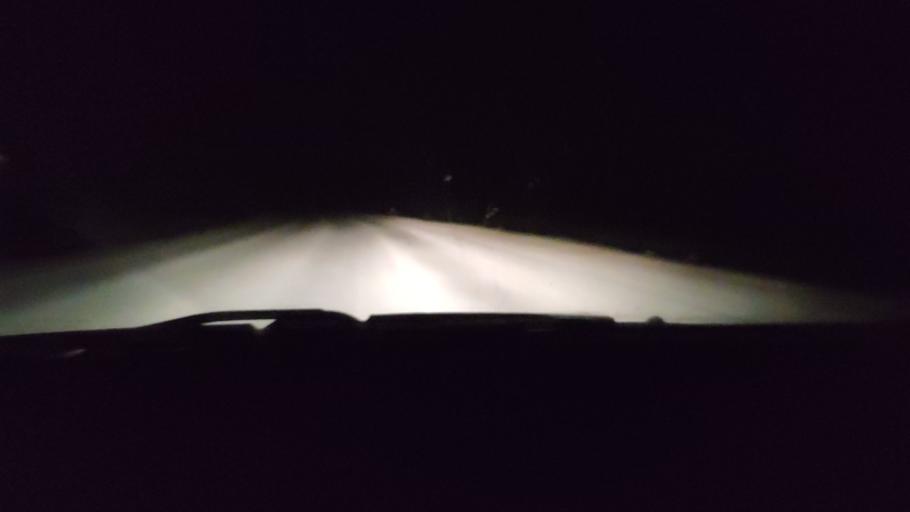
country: RU
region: Saratov
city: Dukhovnitskoye
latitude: 52.7160
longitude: 48.2664
